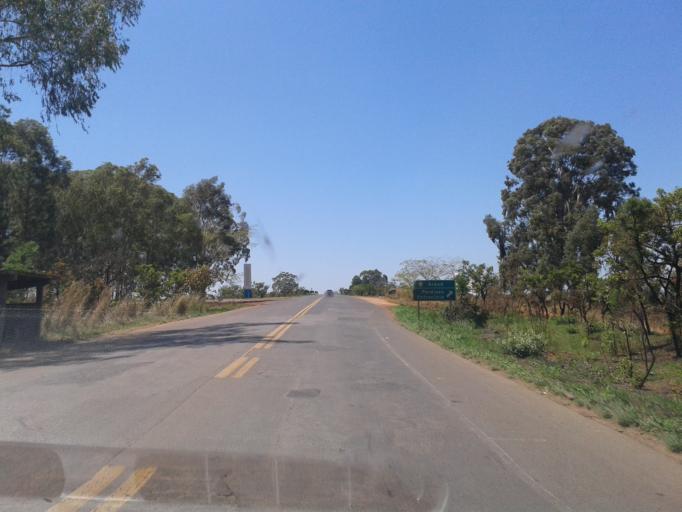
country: BR
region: Minas Gerais
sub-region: Araxa
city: Araxa
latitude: -19.3994
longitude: -47.3226
